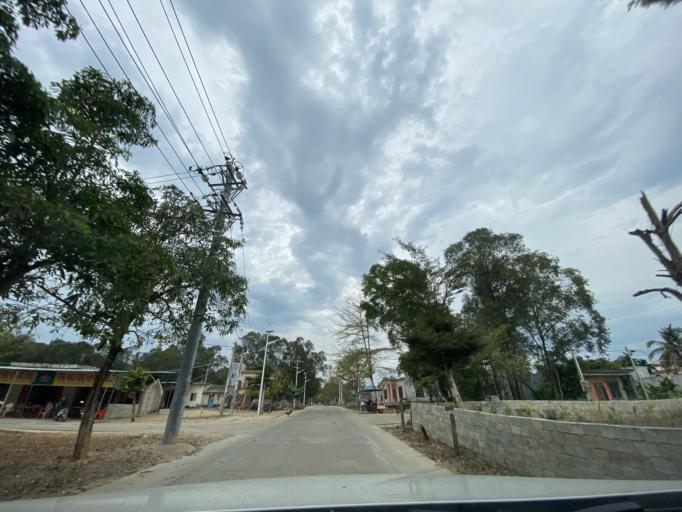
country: CN
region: Hainan
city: Yingzhou
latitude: 18.4197
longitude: 109.8223
